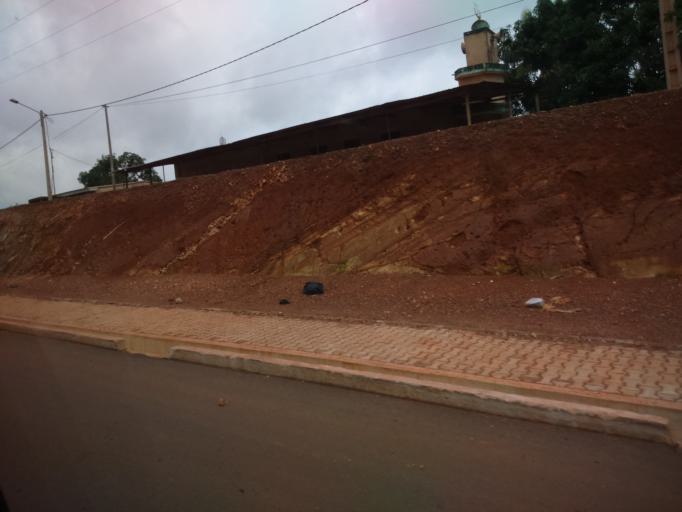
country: CI
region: Moyen-Comoe
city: Abengourou
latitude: 6.7211
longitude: -3.5129
